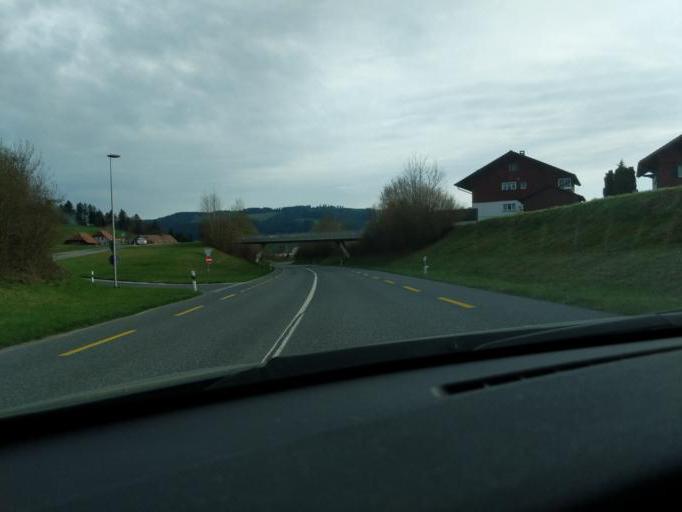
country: CH
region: Bern
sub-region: Emmental District
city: Signau
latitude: 46.9322
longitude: 7.7402
